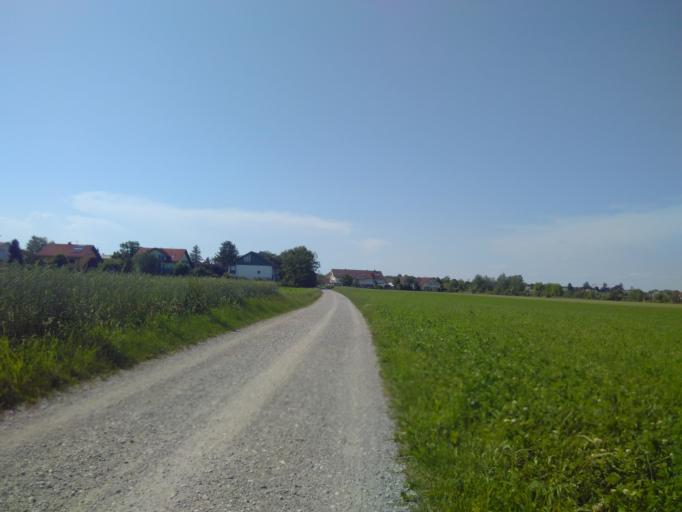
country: DE
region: Bavaria
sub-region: Upper Bavaria
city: Olching
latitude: 48.2008
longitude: 11.3409
